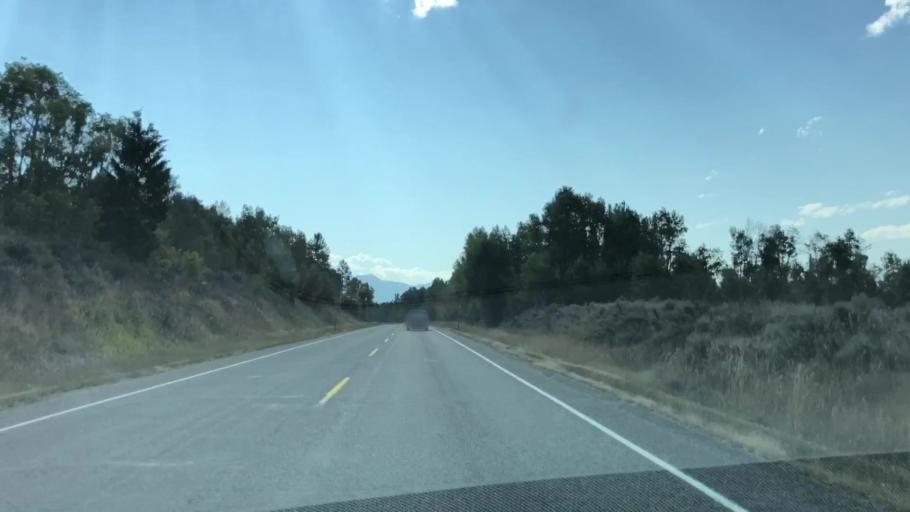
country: US
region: Wyoming
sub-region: Teton County
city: Hoback
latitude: 43.2117
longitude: -111.0599
